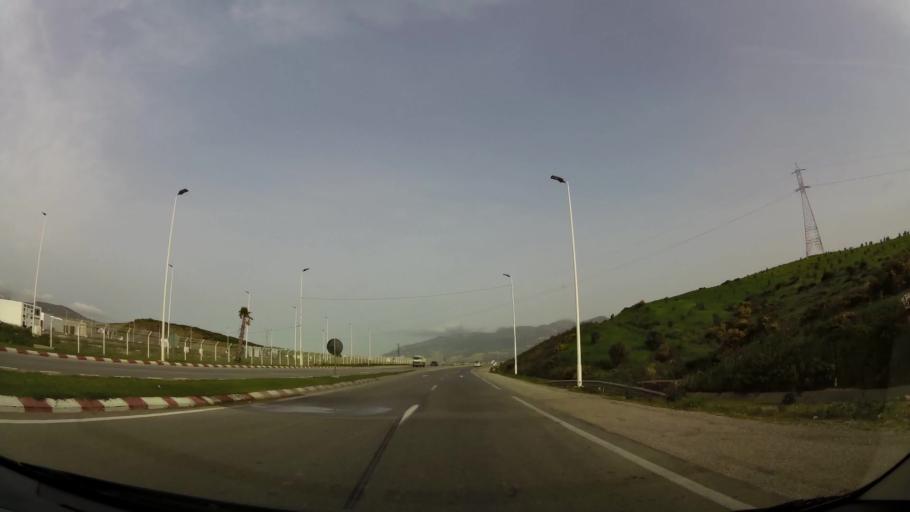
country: MA
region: Tanger-Tetouan
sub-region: Tetouan
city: Saddina
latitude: 35.5633
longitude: -5.4863
